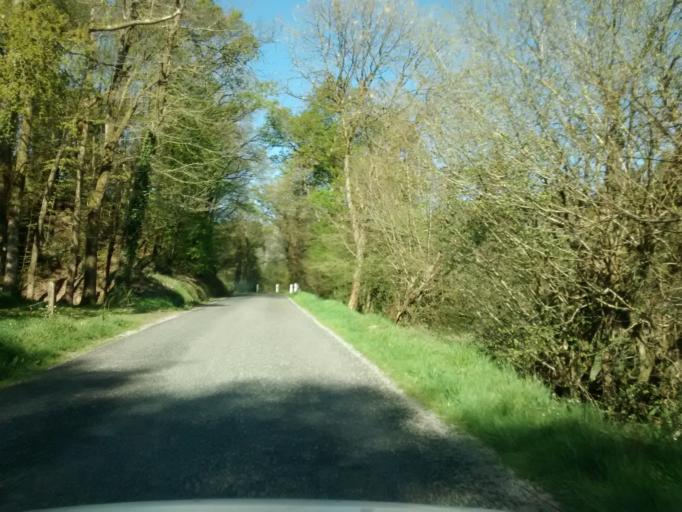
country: FR
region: Brittany
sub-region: Departement du Morbihan
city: Serent
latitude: 47.8708
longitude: -2.5188
